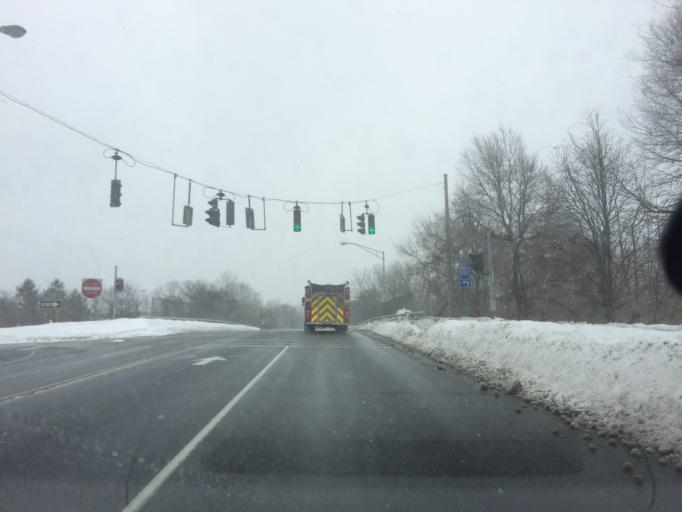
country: US
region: New York
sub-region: Monroe County
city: Brighton
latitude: 43.1267
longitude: -77.5544
